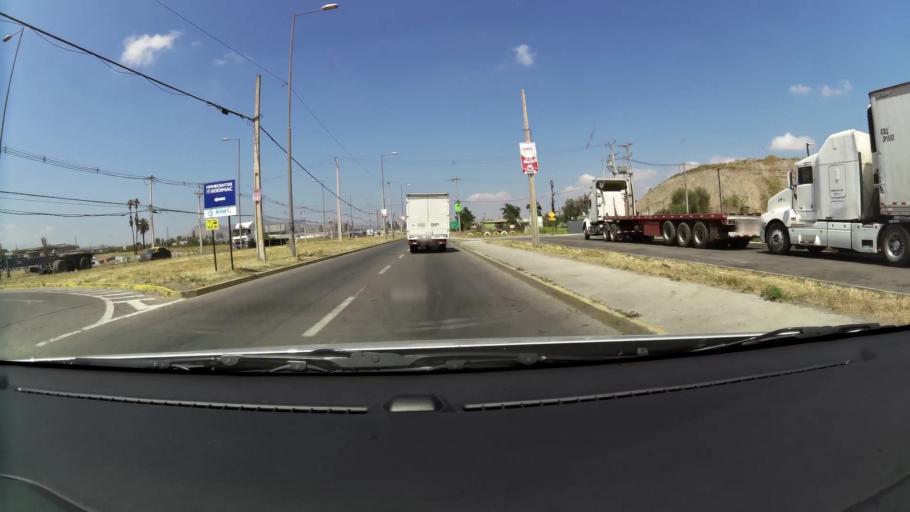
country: CL
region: Santiago Metropolitan
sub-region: Provincia de Santiago
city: Lo Prado
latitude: -33.5201
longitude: -70.7234
